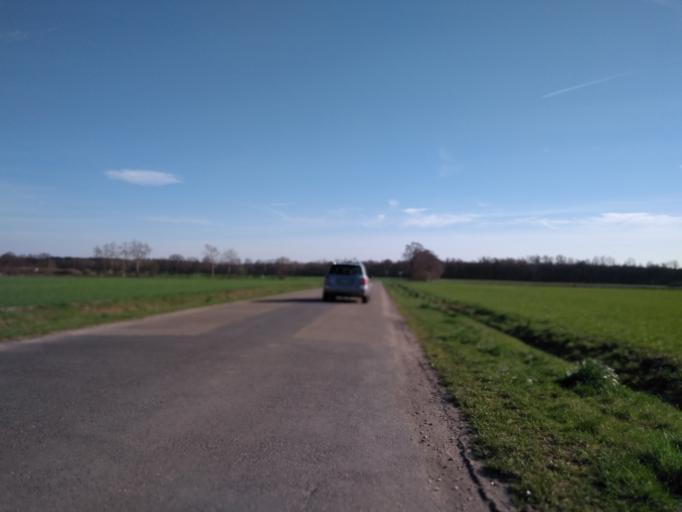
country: DE
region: North Rhine-Westphalia
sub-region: Regierungsbezirk Dusseldorf
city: Hunxe
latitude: 51.6096
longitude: 6.8455
